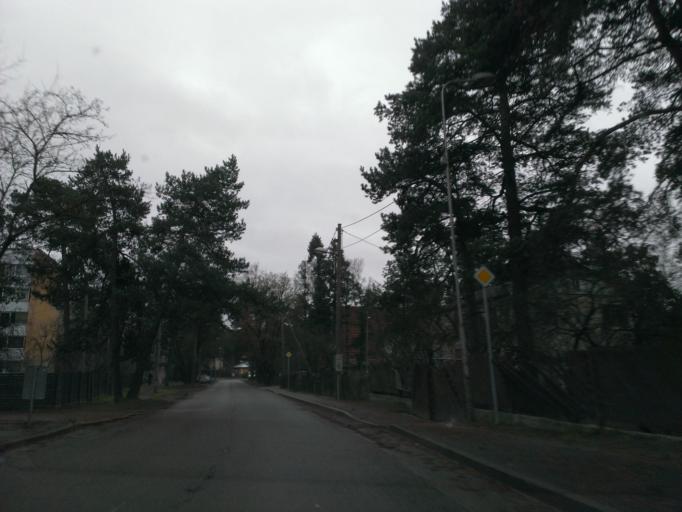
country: LV
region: Riga
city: Bergi
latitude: 56.9990
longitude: 24.2761
